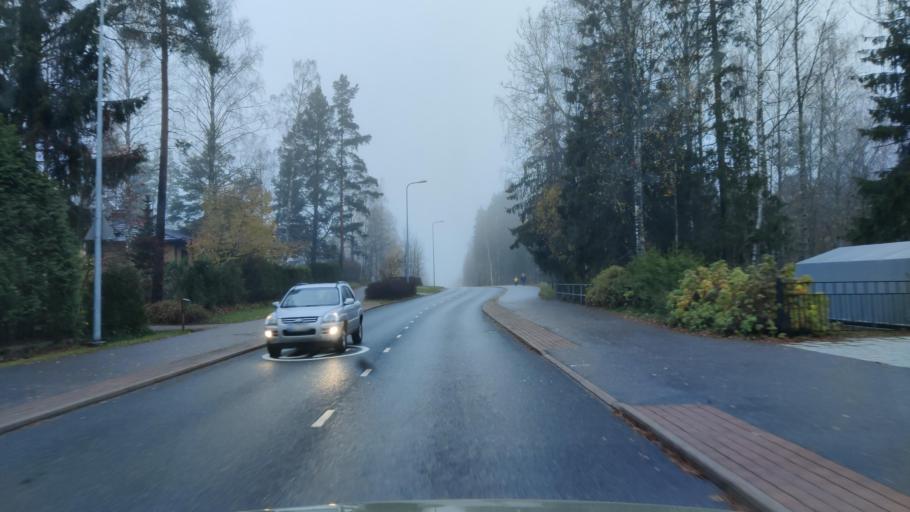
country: FI
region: Uusimaa
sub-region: Helsinki
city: Kerava
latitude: 60.3591
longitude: 25.0951
